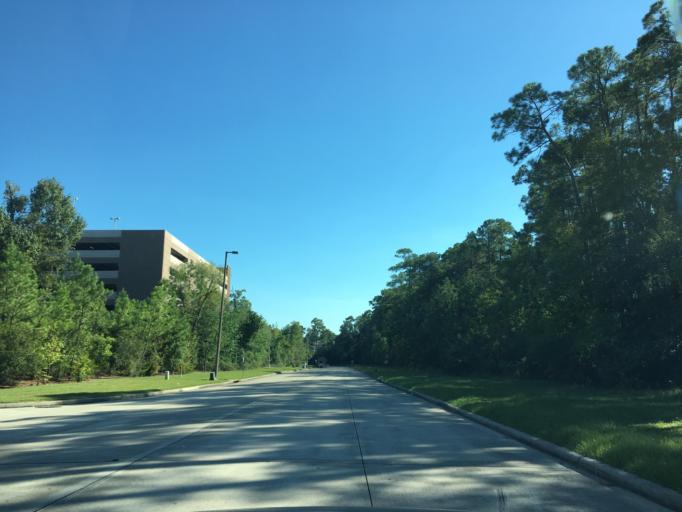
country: US
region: Texas
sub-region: Montgomery County
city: Shenandoah
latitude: 30.2025
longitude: -95.4595
